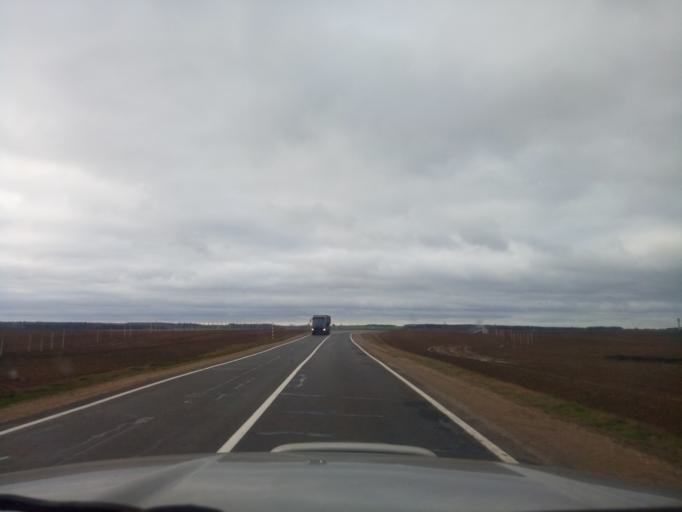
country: BY
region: Minsk
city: Kapyl'
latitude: 53.2016
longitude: 27.2167
